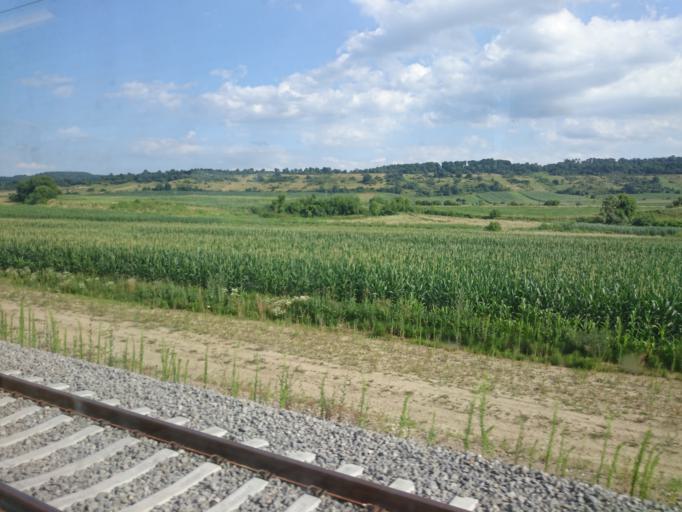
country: RO
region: Sibiu
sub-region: Comuna Laslea
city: Laslea
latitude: 46.2206
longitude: 24.6435
